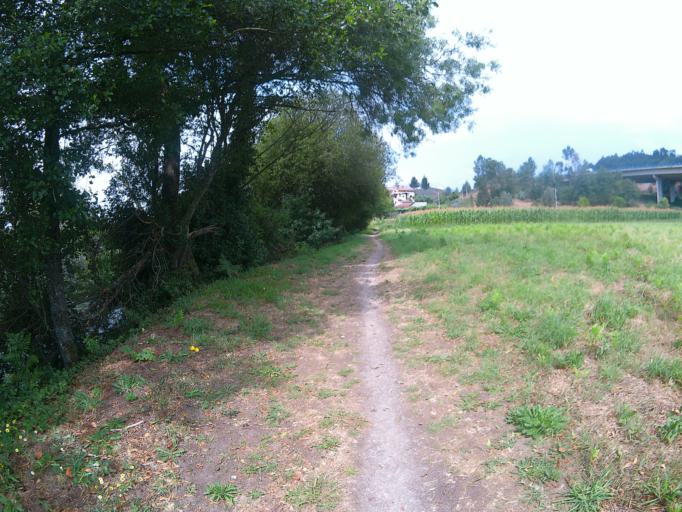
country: PT
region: Viana do Castelo
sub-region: Ponte de Lima
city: Ponte de Lima
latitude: 41.7779
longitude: -8.5667
